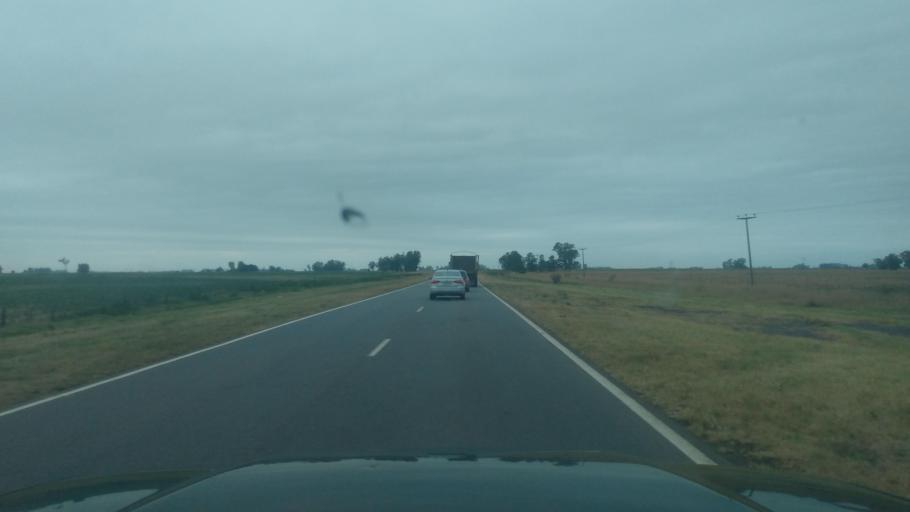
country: AR
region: Buenos Aires
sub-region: Partido de Nueve de Julio
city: Nueve de Julio
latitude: -35.3986
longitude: -60.7553
